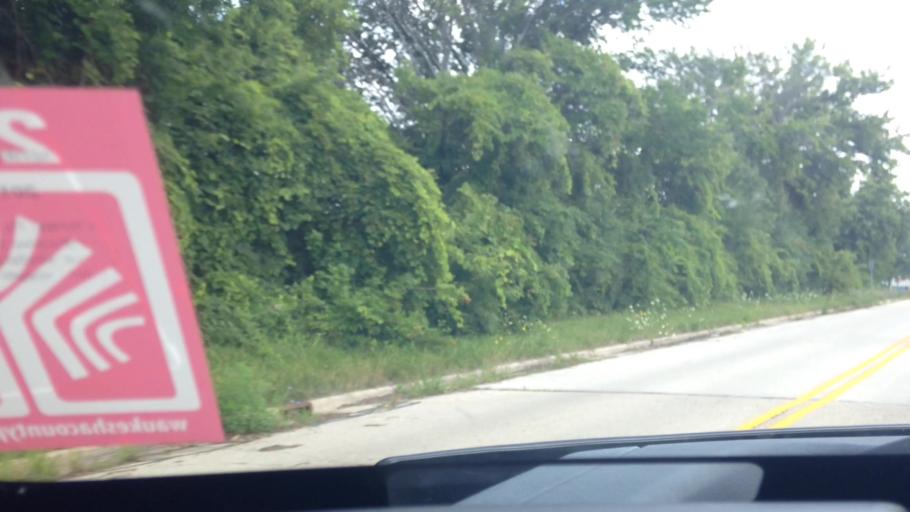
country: US
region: Wisconsin
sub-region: Waukesha County
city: Menomonee Falls
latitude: 43.1893
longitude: -88.1404
